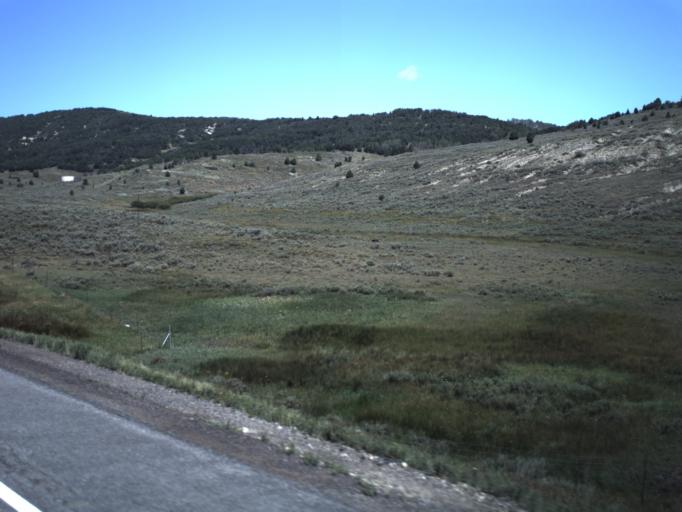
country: US
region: Utah
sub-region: Carbon County
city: Helper
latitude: 39.9260
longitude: -111.0717
